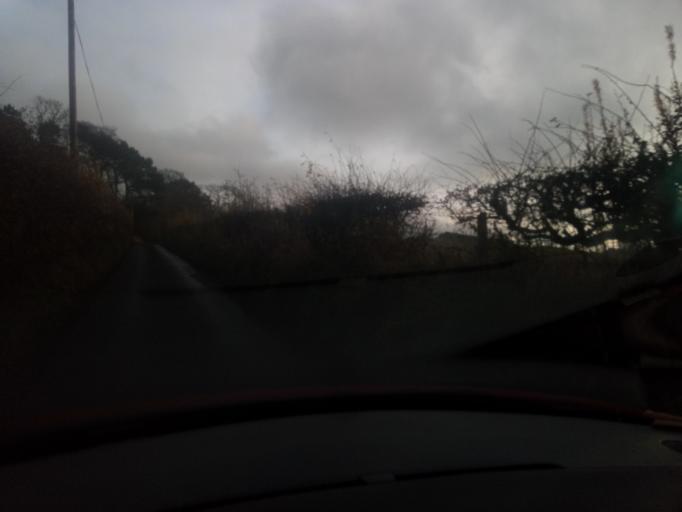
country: GB
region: Scotland
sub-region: The Scottish Borders
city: Jedburgh
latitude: 55.4853
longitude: -2.6097
